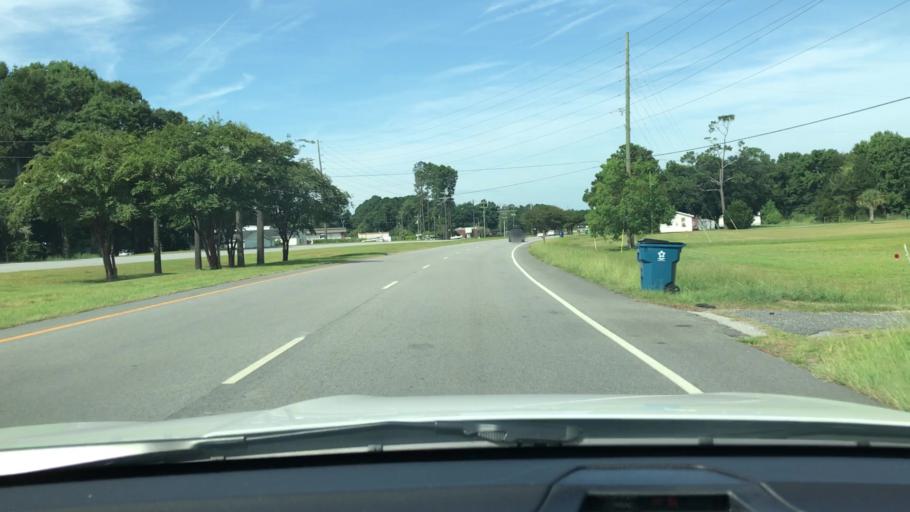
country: US
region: South Carolina
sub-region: Charleston County
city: Isle of Palms
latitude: 32.8843
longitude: -79.7500
